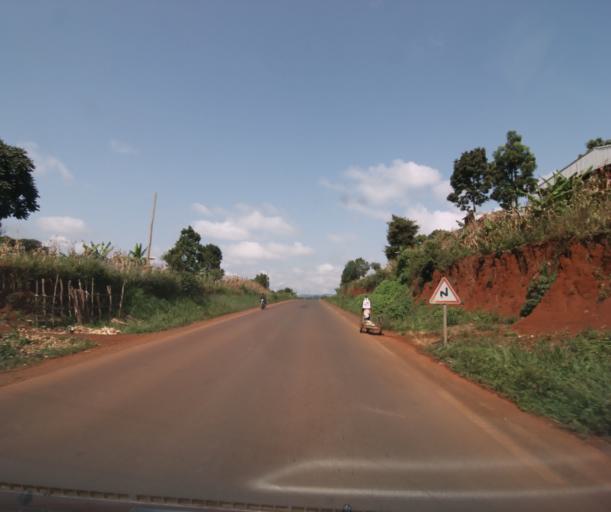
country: CM
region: West
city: Bansoa
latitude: 5.4959
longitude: 10.2288
